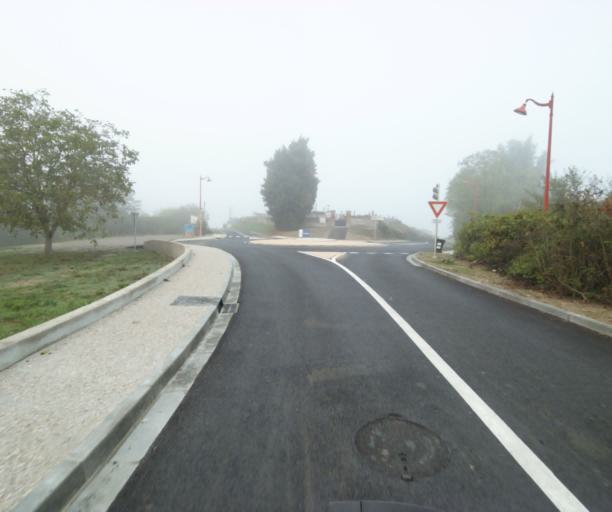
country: FR
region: Midi-Pyrenees
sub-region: Departement du Tarn-et-Garonne
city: Saint-Nauphary
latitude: 43.9346
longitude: 1.4640
